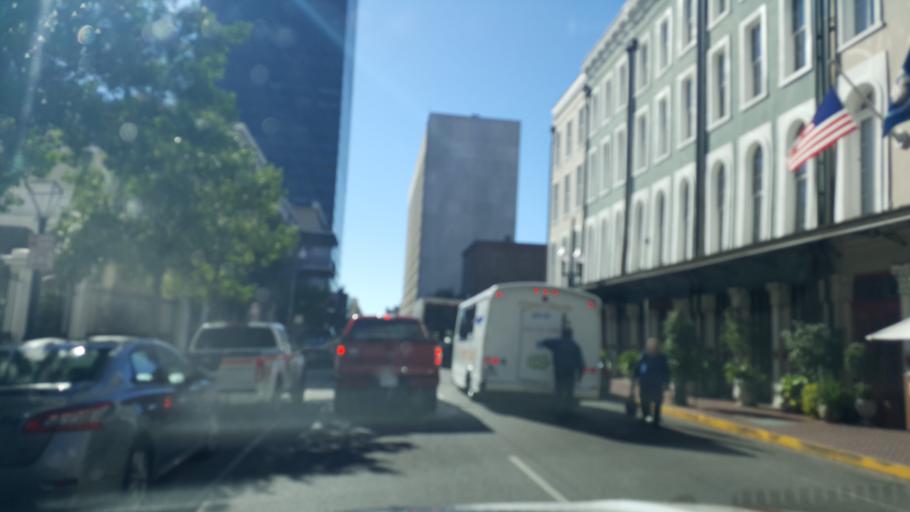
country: US
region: Louisiana
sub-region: Orleans Parish
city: New Orleans
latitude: 29.9503
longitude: -90.0677
